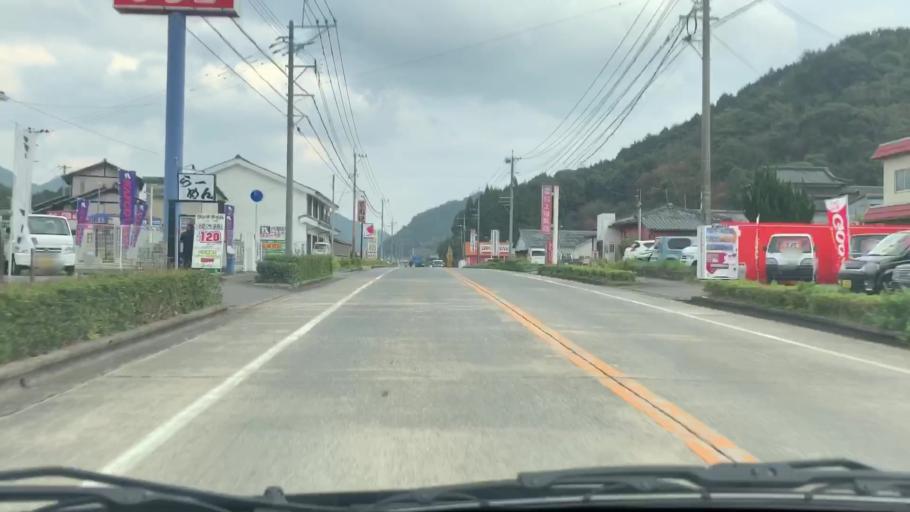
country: JP
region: Saga Prefecture
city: Imaricho-ko
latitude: 33.1840
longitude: 129.8727
